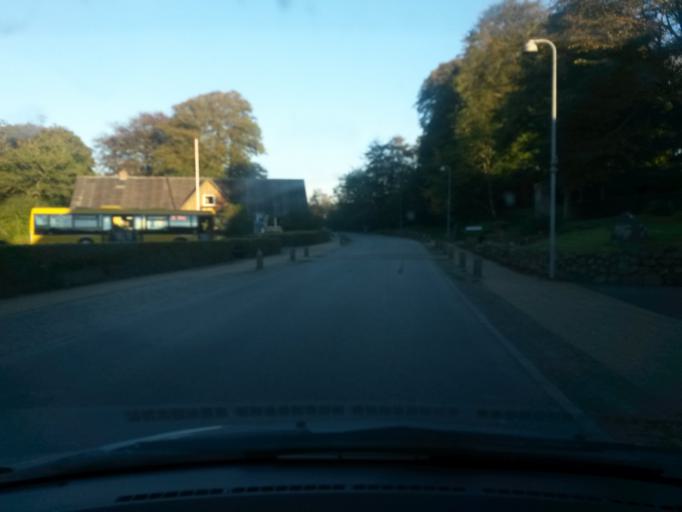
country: DK
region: Central Jutland
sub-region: Silkeborg Kommune
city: Kjellerup
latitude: 56.2858
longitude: 9.3333
